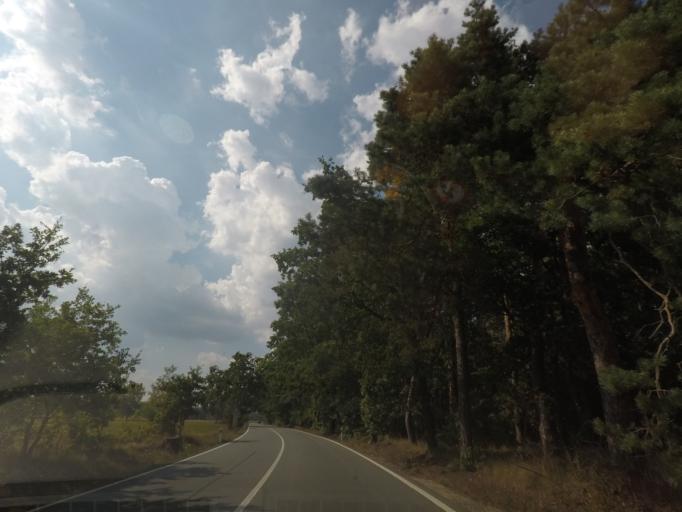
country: CZ
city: Albrechtice nad Orlici
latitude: 50.1316
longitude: 16.0618
